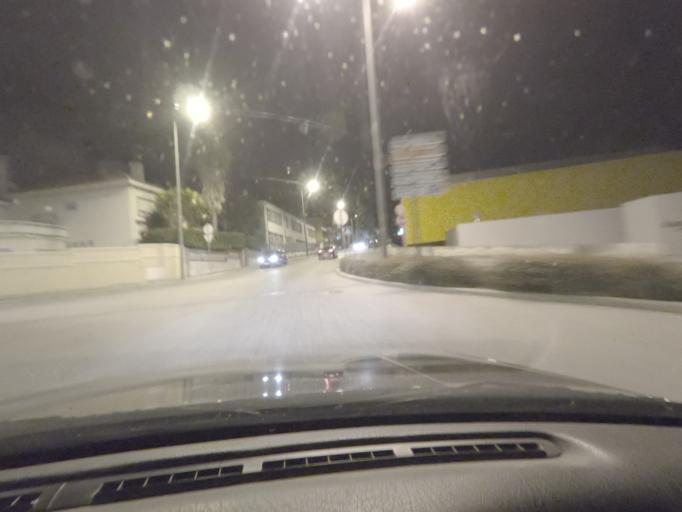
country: PT
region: Vila Real
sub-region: Peso da Regua
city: Peso da Regua
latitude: 41.1652
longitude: -7.7922
